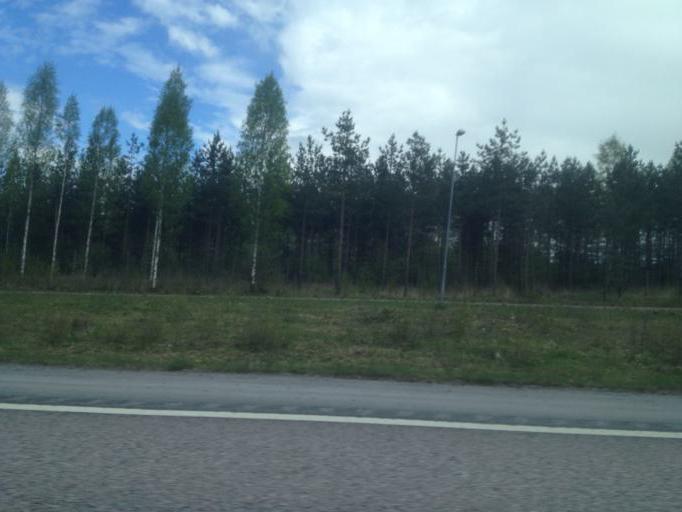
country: FI
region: Haeme
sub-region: Riihimaeki
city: Riihimaeki
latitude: 60.6618
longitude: 24.7924
